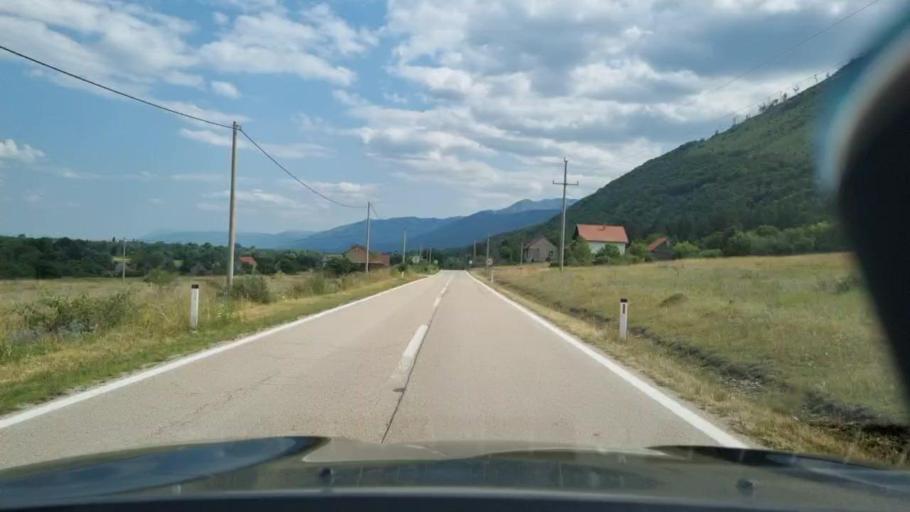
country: BA
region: Federation of Bosnia and Herzegovina
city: Bosansko Grahovo
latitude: 44.0590
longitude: 16.5839
